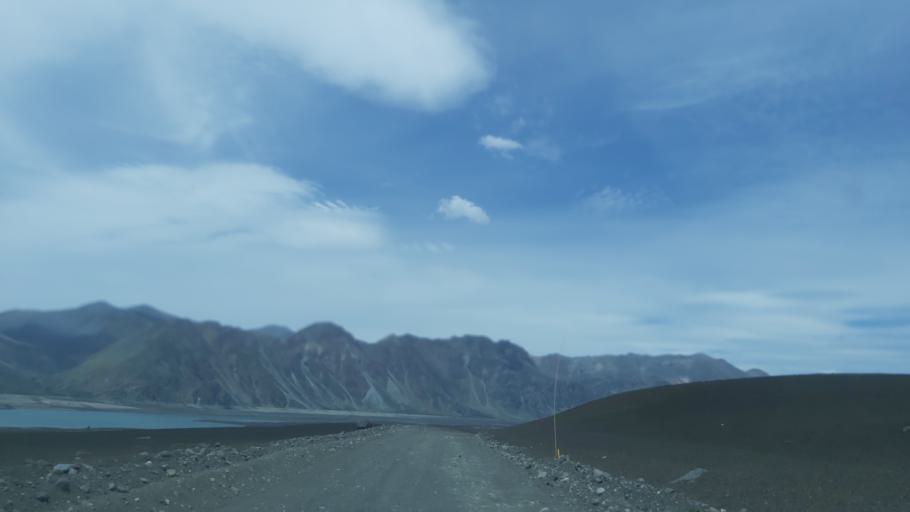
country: AR
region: Neuquen
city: Andacollo
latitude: -37.4210
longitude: -71.2886
